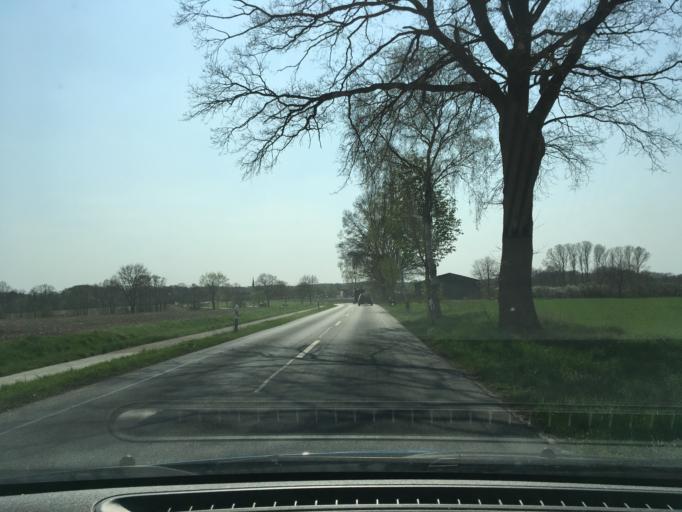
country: DE
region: Lower Saxony
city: Kirchgellersen
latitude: 53.2395
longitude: 10.3004
